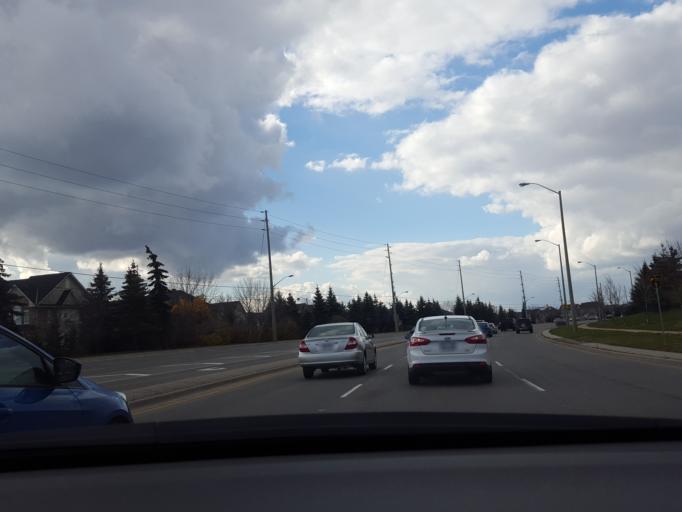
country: CA
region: Ontario
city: Brampton
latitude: 43.6327
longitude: -79.7232
